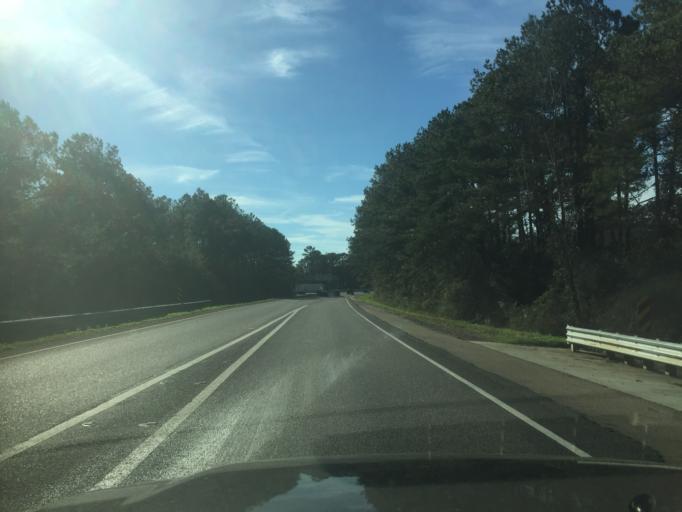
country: US
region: Louisiana
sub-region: Saint Tammany Parish
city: Slidell
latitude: 30.3086
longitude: -89.7435
